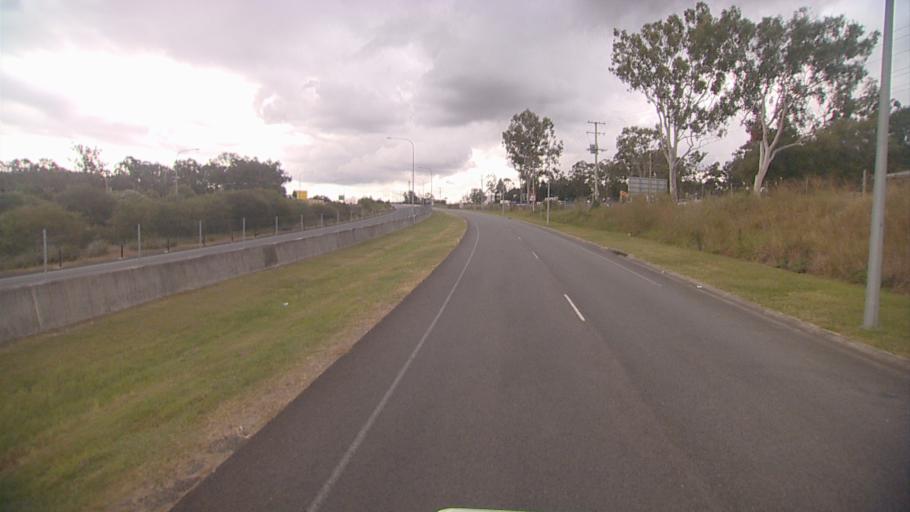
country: AU
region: Queensland
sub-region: Logan
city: Park Ridge South
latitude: -27.7110
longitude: 153.0377
